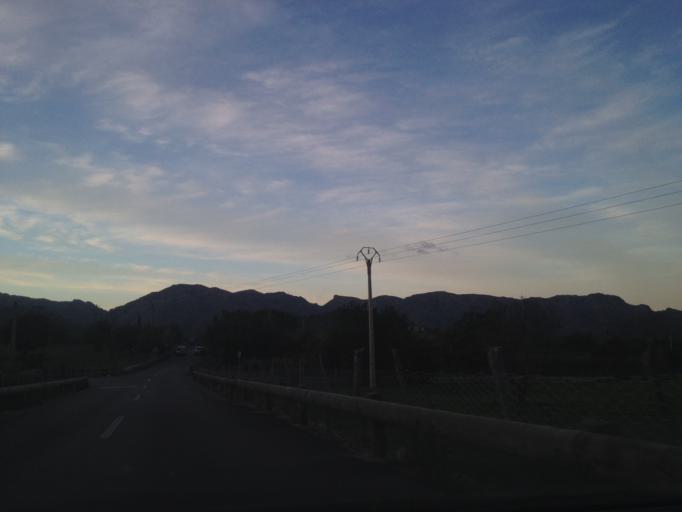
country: ES
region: Balearic Islands
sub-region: Illes Balears
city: Pollenca
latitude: 39.8649
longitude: 3.0430
